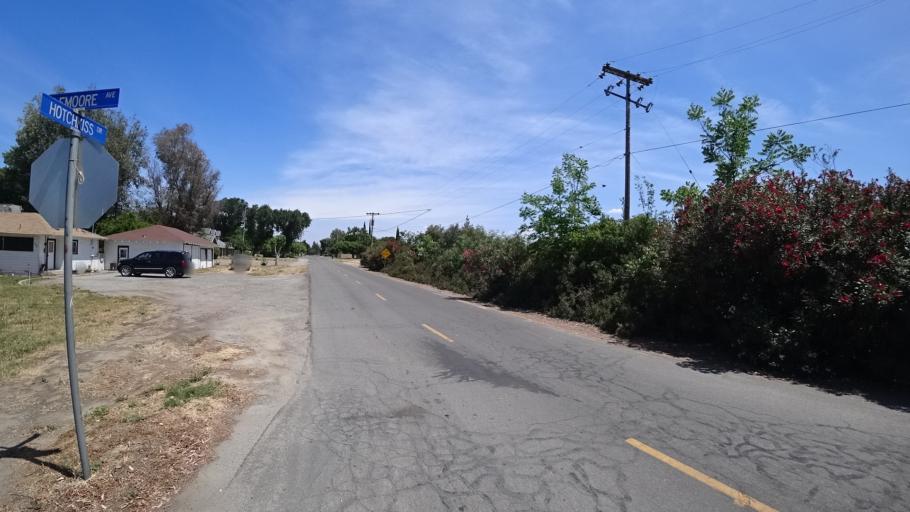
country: US
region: California
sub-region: Kings County
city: Lemoore
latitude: 36.2873
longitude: -119.7807
